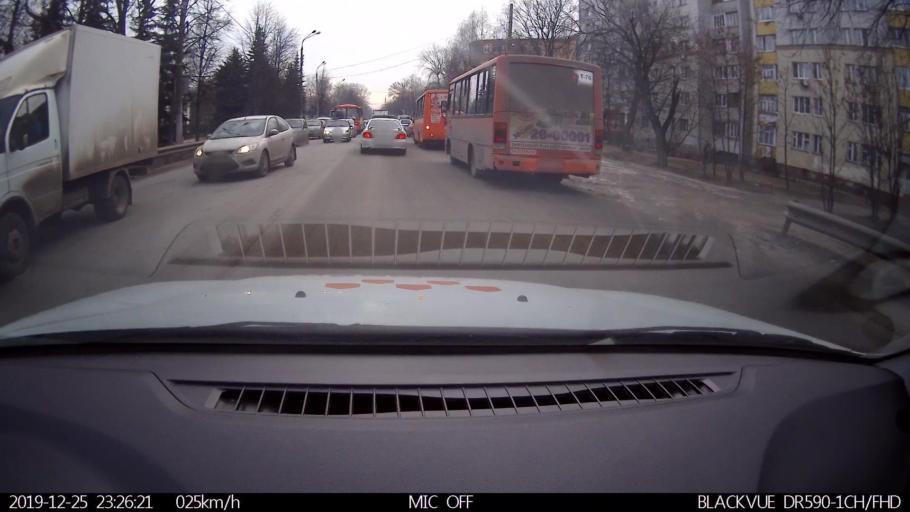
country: RU
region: Nizjnij Novgorod
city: Gorbatovka
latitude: 56.3453
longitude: 43.8402
